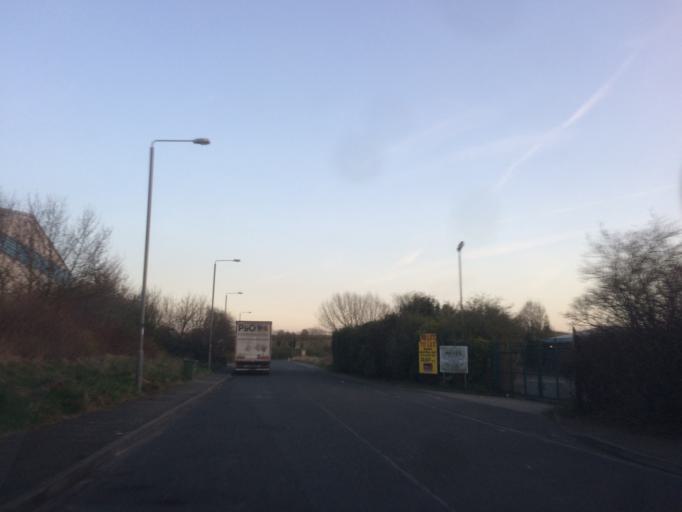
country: GB
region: England
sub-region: City and Borough of Wakefield
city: Ferrybridge
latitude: 53.7033
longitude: -1.2748
